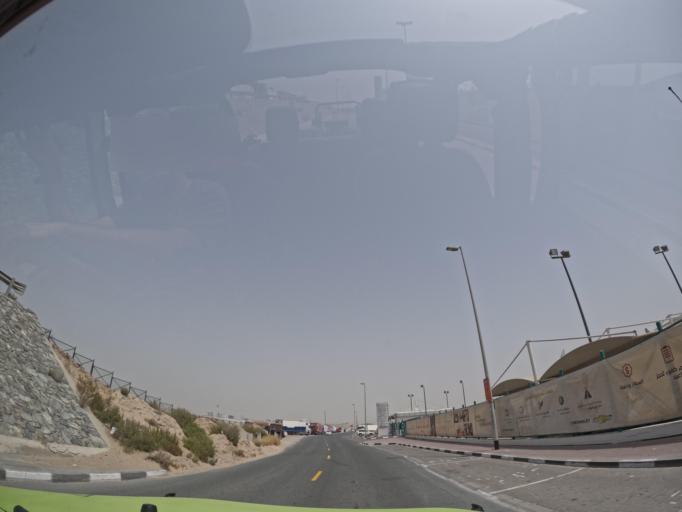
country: AE
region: Ash Shariqah
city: Sharjah
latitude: 25.1885
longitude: 55.3740
